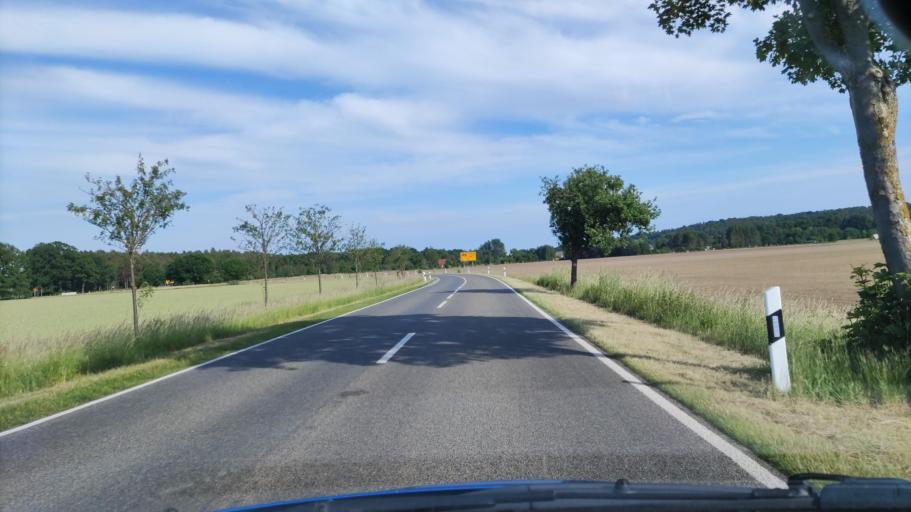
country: DE
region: Saxony-Anhalt
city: Kalbe
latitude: 52.6043
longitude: 11.3195
